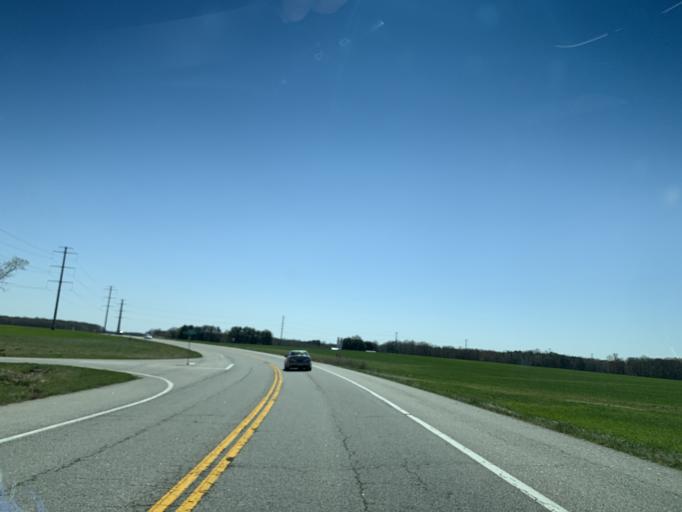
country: US
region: Maryland
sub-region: Queen Anne's County
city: Centreville
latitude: 38.9964
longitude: -76.0476
